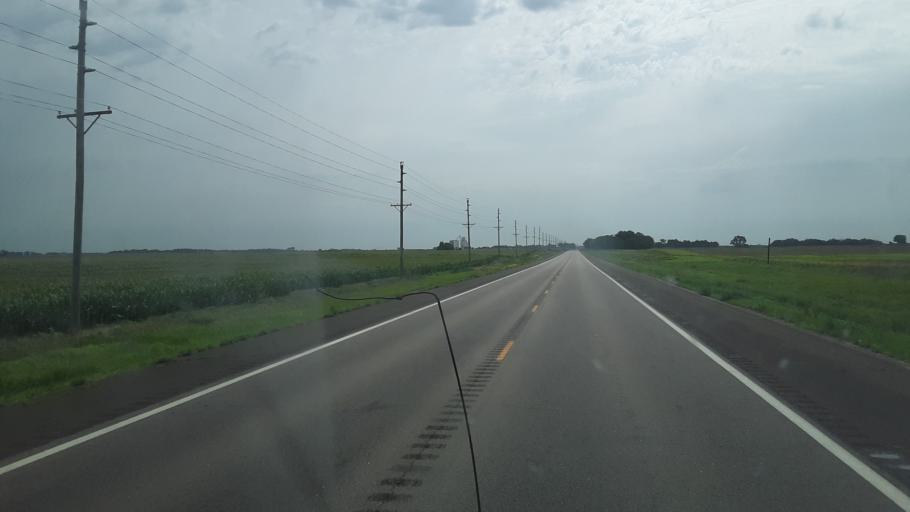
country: US
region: Kansas
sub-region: Stafford County
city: Stafford
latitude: 37.9551
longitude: -98.5260
